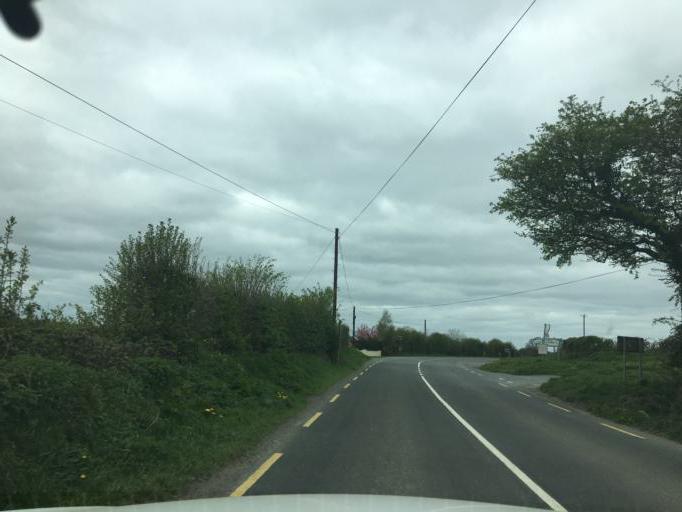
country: IE
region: Leinster
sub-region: Loch Garman
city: New Ross
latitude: 52.4497
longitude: -6.9814
